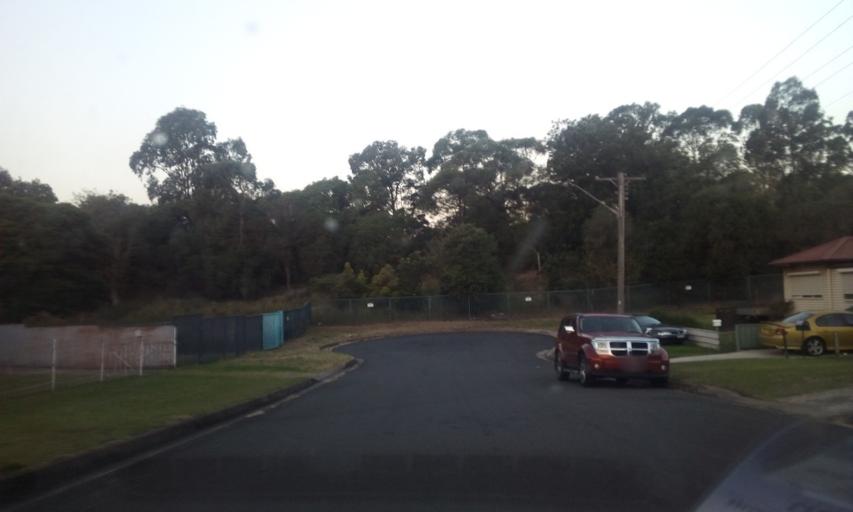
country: AU
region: New South Wales
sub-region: Wollongong
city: Cringila
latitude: -34.4710
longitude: 150.8740
